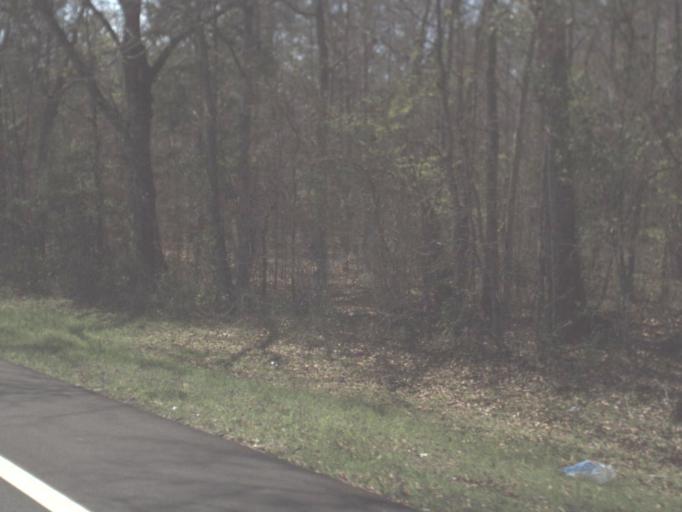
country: US
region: Florida
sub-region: Jackson County
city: Sneads
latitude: 30.7341
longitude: -85.0199
